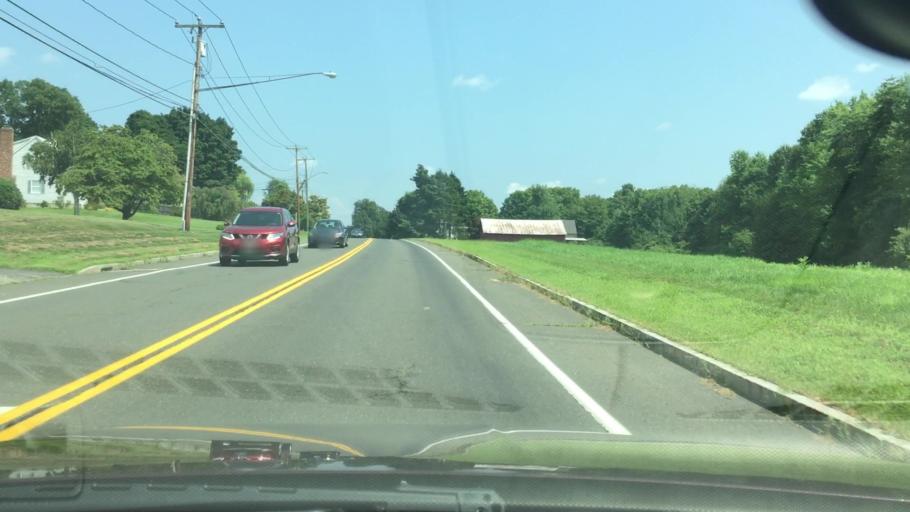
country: US
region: Connecticut
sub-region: Hartford County
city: East Hartford
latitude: 41.7906
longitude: -72.5772
